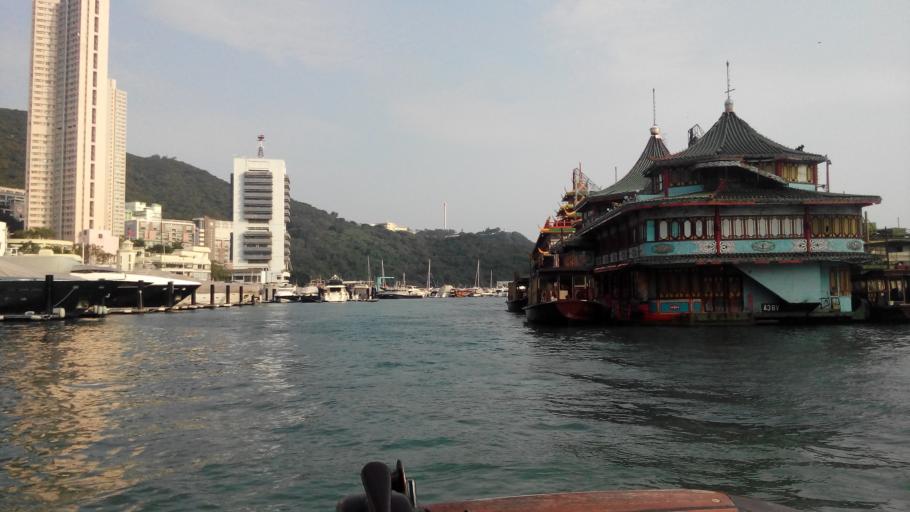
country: HK
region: Central and Western
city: Central
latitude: 22.2447
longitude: 114.1612
